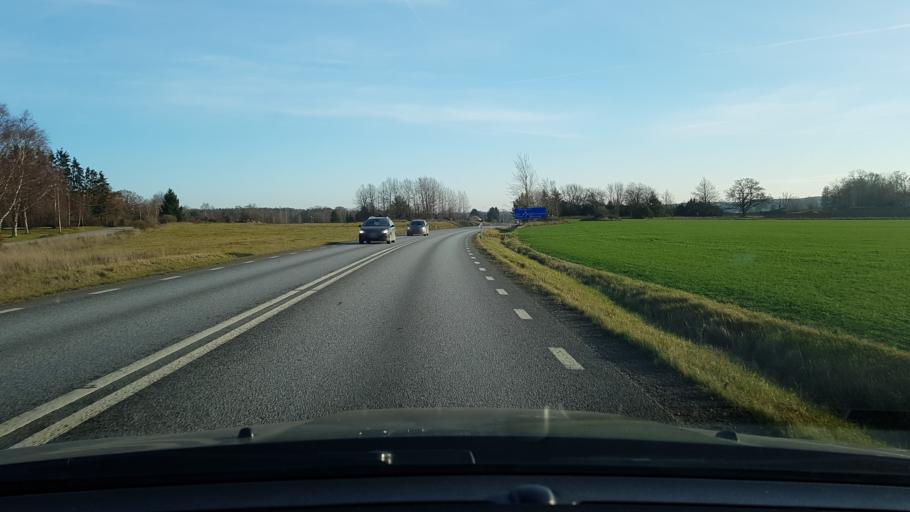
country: SE
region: Stockholm
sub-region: Vallentuna Kommun
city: Vallentuna
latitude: 59.7534
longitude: 18.0375
